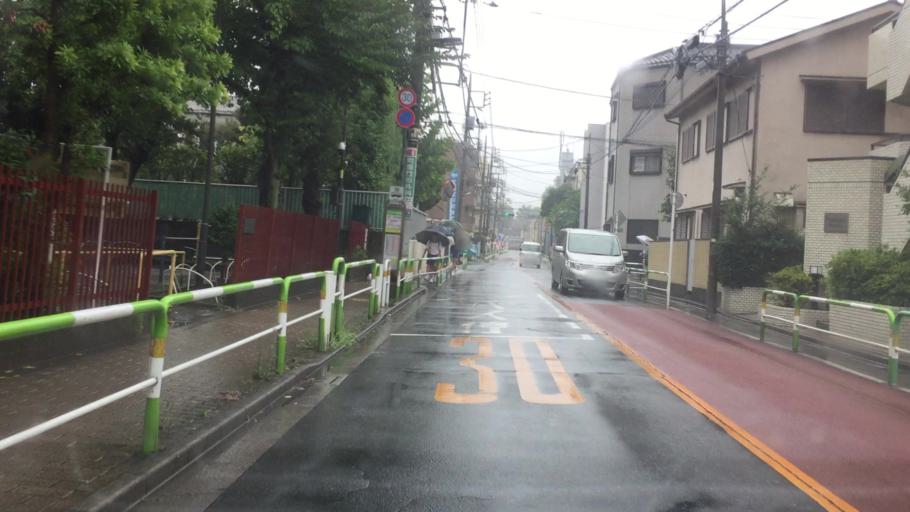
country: JP
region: Saitama
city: Soka
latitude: 35.7465
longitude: 139.7863
